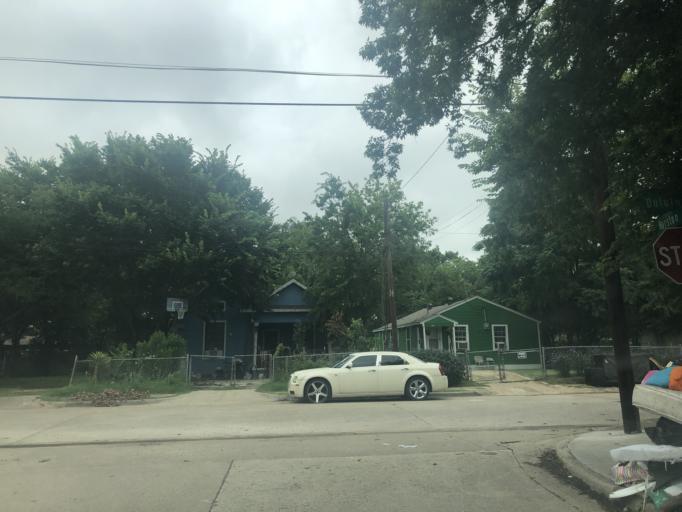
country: US
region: Texas
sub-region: Dallas County
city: Dallas
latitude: 32.7761
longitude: -96.8500
